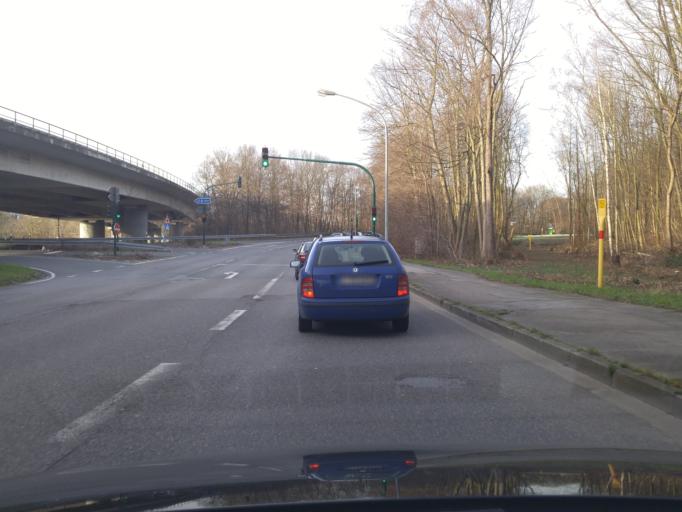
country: DE
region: North Rhine-Westphalia
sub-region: Regierungsbezirk Dusseldorf
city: Velbert
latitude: 51.4043
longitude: 7.0844
